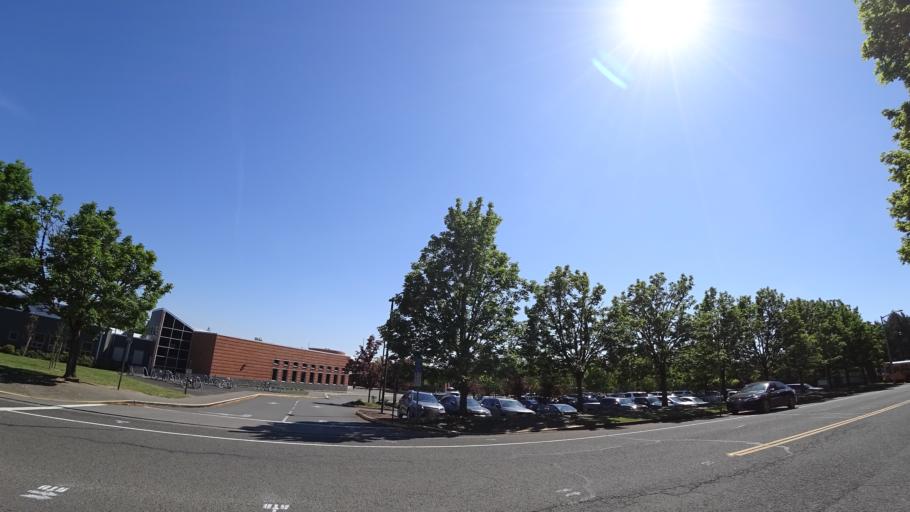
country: US
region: Oregon
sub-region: Washington County
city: Tigard
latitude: 45.4477
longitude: -122.8027
